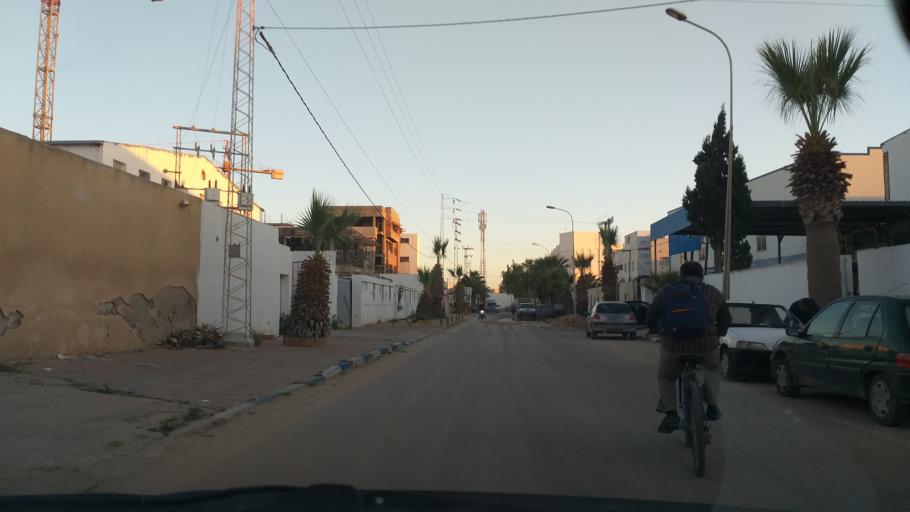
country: TN
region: Safaqis
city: Al Qarmadah
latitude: 34.7629
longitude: 10.7785
